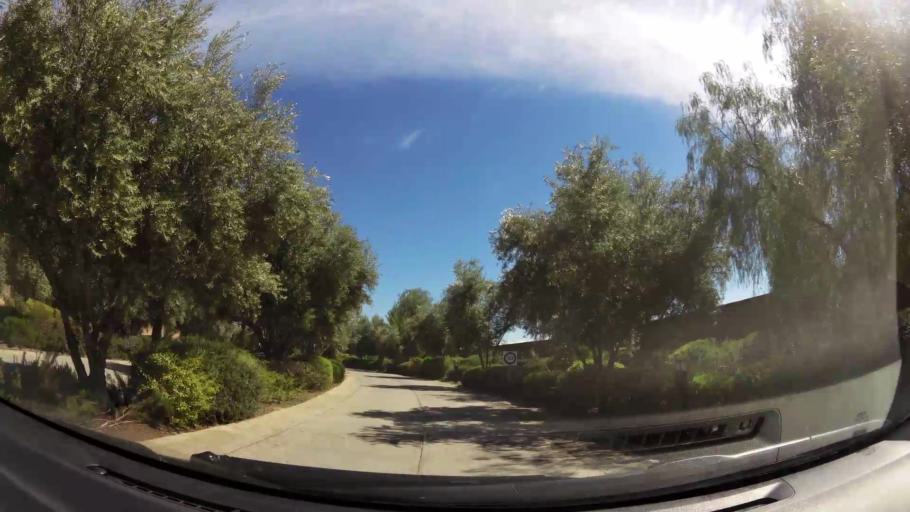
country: MA
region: Marrakech-Tensift-Al Haouz
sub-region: Marrakech
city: Marrakesh
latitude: 31.6044
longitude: -7.9545
